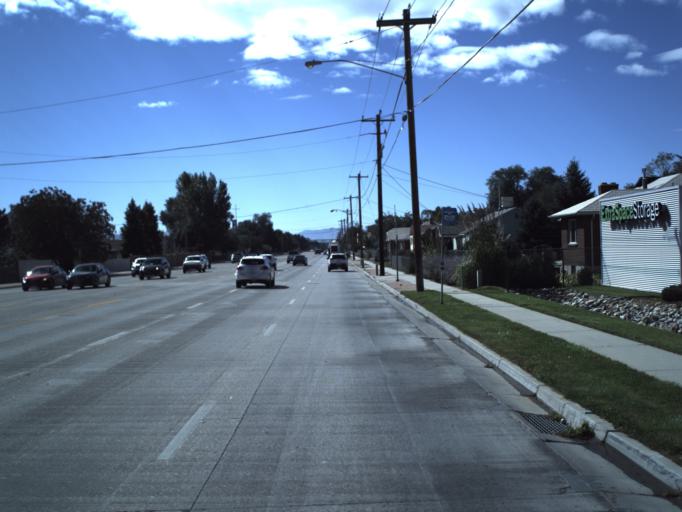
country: US
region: Utah
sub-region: Salt Lake County
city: West Jordan
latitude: 40.6203
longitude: -111.9389
